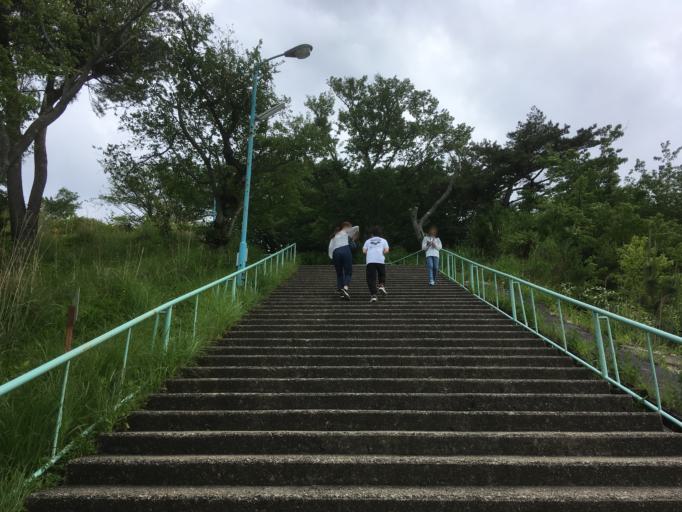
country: JP
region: Nara
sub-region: Ikoma-shi
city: Ikoma
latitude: 34.6813
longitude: 135.6771
